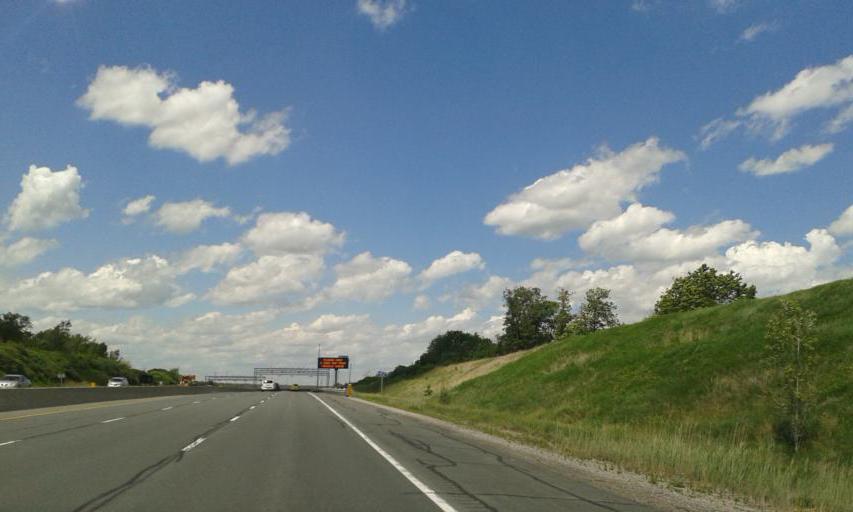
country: CA
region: Ontario
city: Burlington
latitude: 43.3672
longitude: -79.8320
